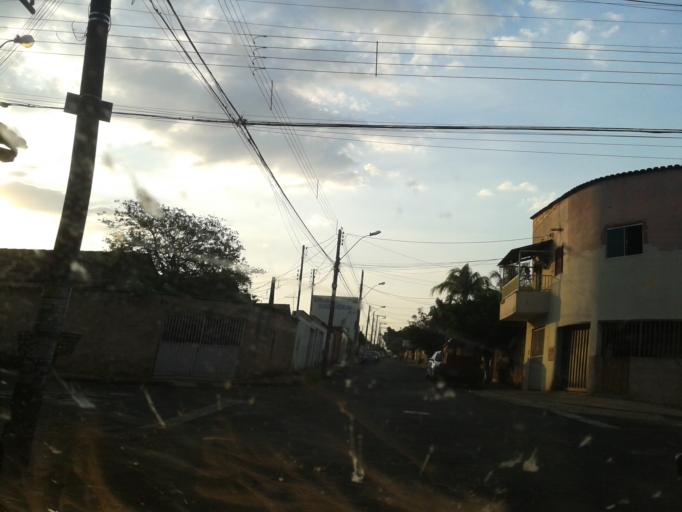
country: BR
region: Minas Gerais
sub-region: Uberlandia
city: Uberlandia
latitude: -18.9174
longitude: -48.3310
